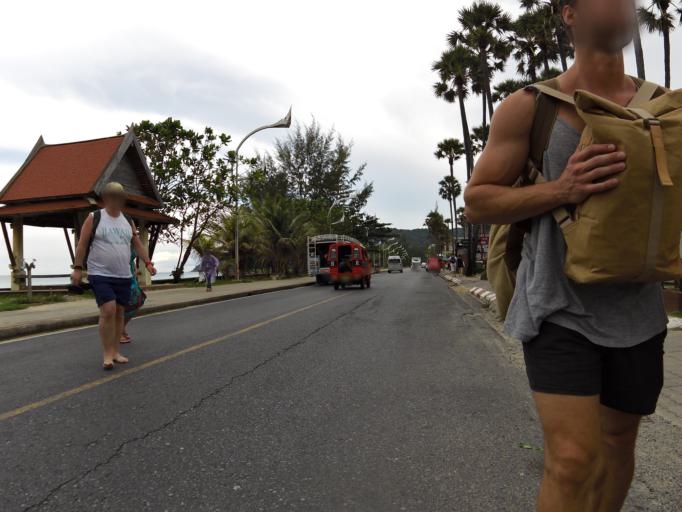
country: TH
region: Phuket
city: Ban Karon
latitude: 7.8435
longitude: 98.2943
